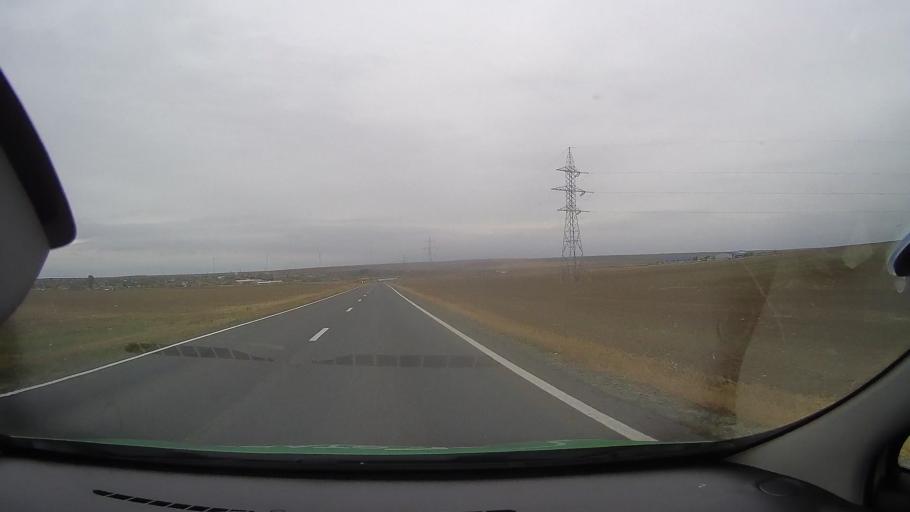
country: RO
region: Constanta
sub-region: Comuna Nicolae Balcescu
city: Dorobantu
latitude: 44.4185
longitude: 28.3138
